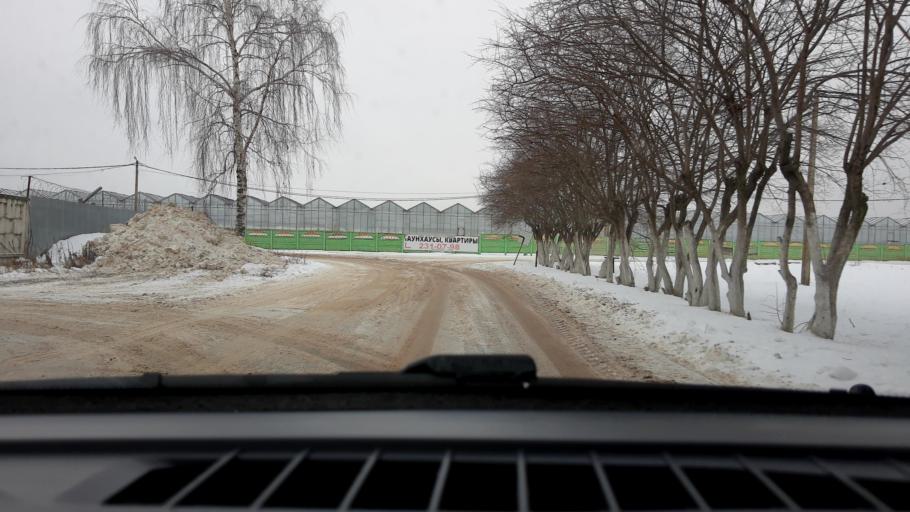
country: RU
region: Nizjnij Novgorod
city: Afonino
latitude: 56.2162
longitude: 44.1003
